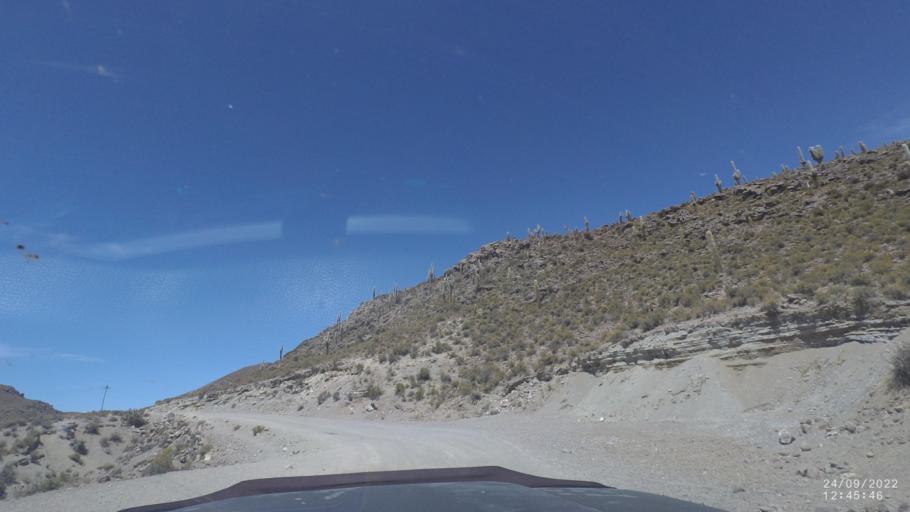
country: BO
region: Potosi
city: Colchani
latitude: -19.8008
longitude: -67.5751
